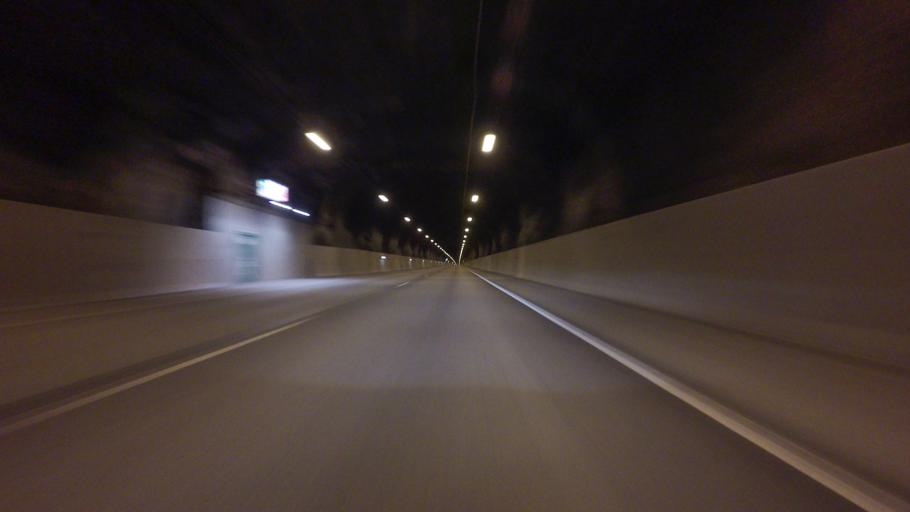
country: FI
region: Uusimaa
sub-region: Helsinki
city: Lohja
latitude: 60.3099
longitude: 24.0190
